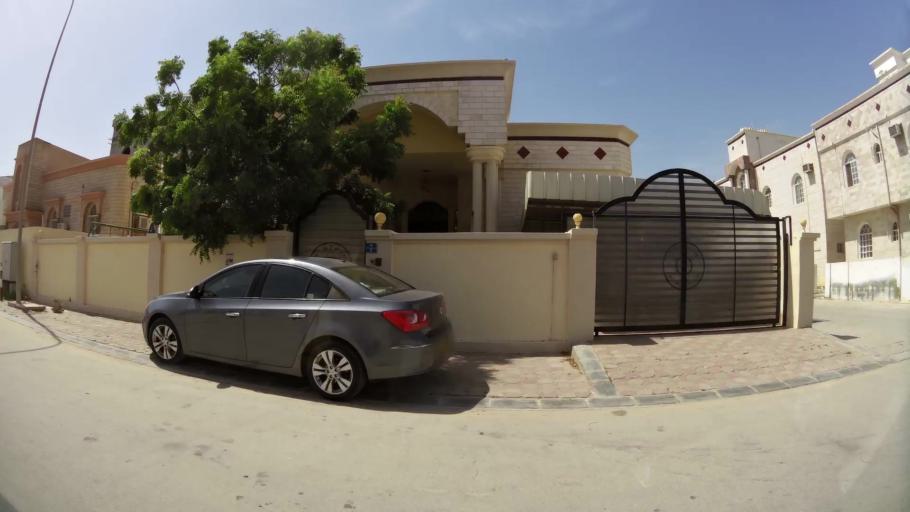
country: OM
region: Zufar
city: Salalah
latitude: 17.0393
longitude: 54.1525
